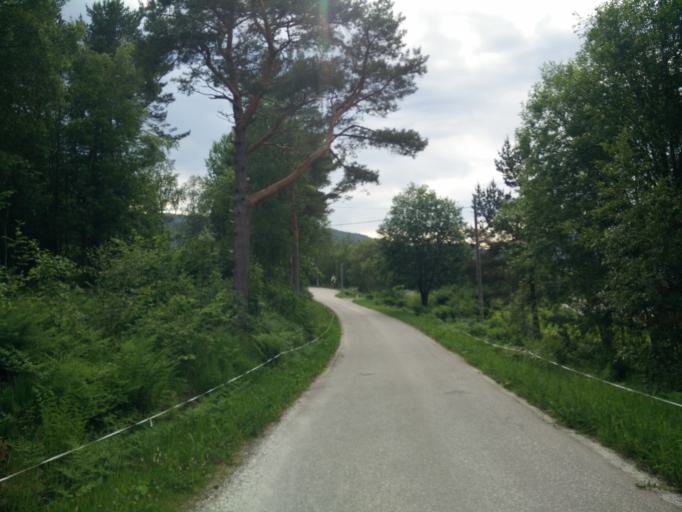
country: NO
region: More og Romsdal
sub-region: Kristiansund
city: Rensvik
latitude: 63.0428
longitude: 7.9684
